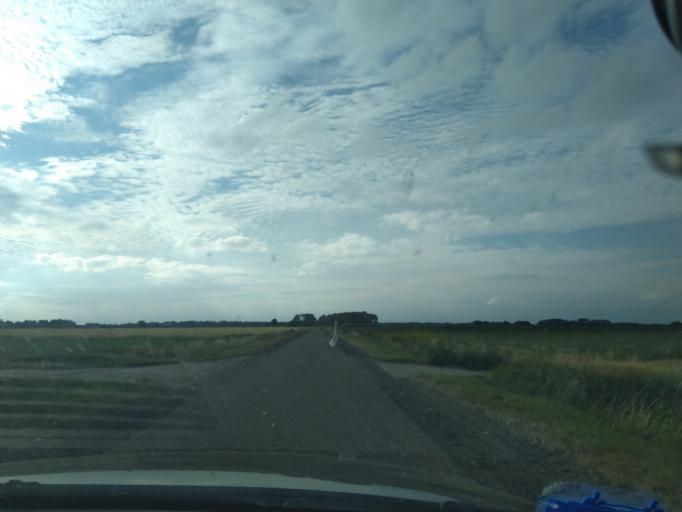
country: NL
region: Groningen
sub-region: Gemeente Vlagtwedde
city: Vlagtwedde
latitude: 53.0832
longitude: 7.1086
